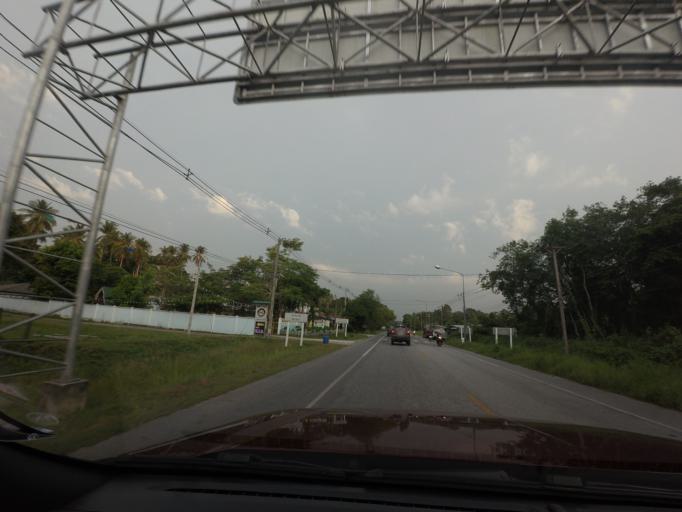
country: TH
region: Pattani
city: Mae Lan
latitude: 6.5994
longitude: 101.1942
